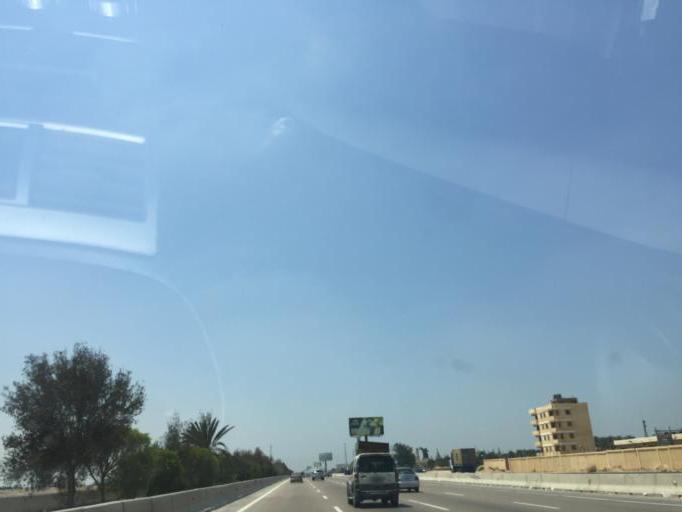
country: EG
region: Al Buhayrah
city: Beheira
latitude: 30.4116
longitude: 30.3577
